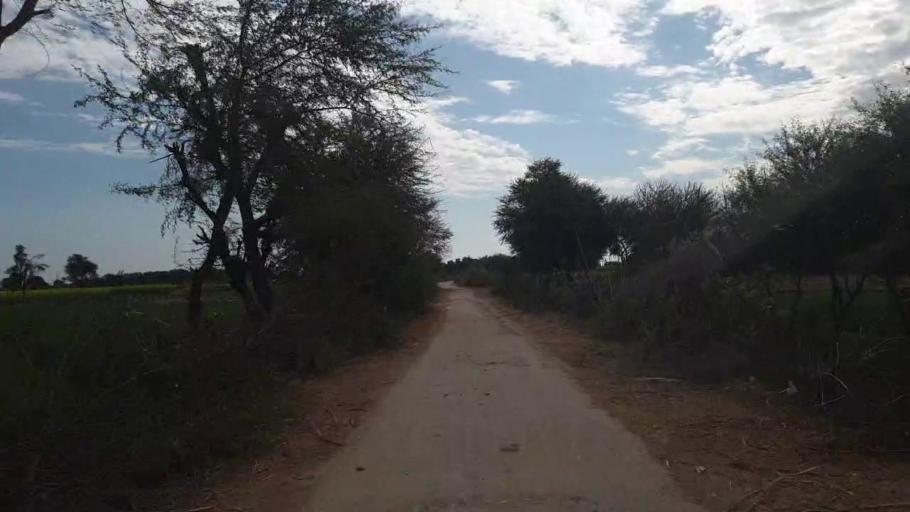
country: PK
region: Sindh
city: Jhol
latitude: 25.9883
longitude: 68.8995
